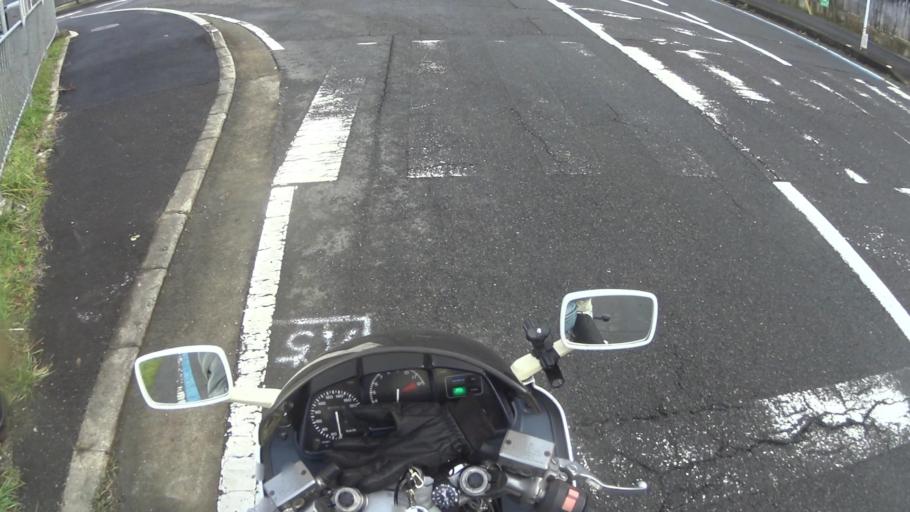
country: JP
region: Kyoto
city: Miyazu
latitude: 35.4233
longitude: 135.2196
